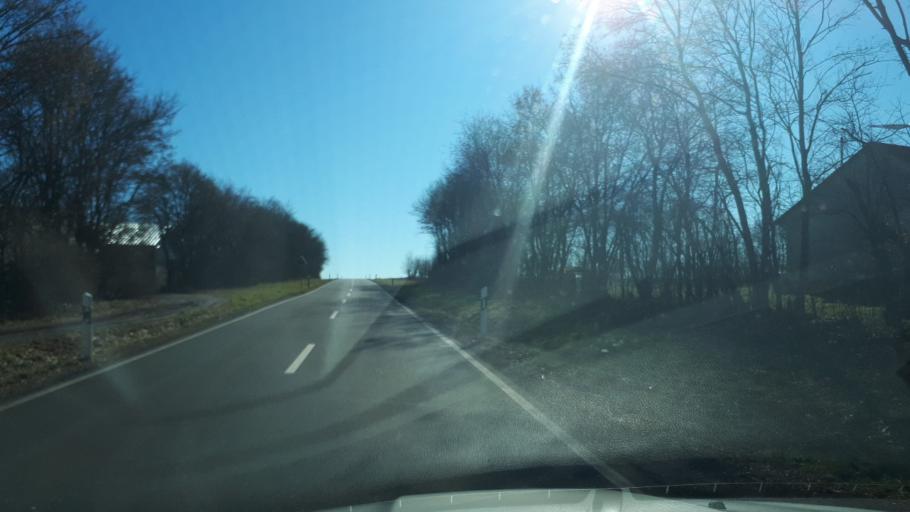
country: DE
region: Rheinland-Pfalz
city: Muckeln
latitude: 50.0941
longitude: 6.9157
